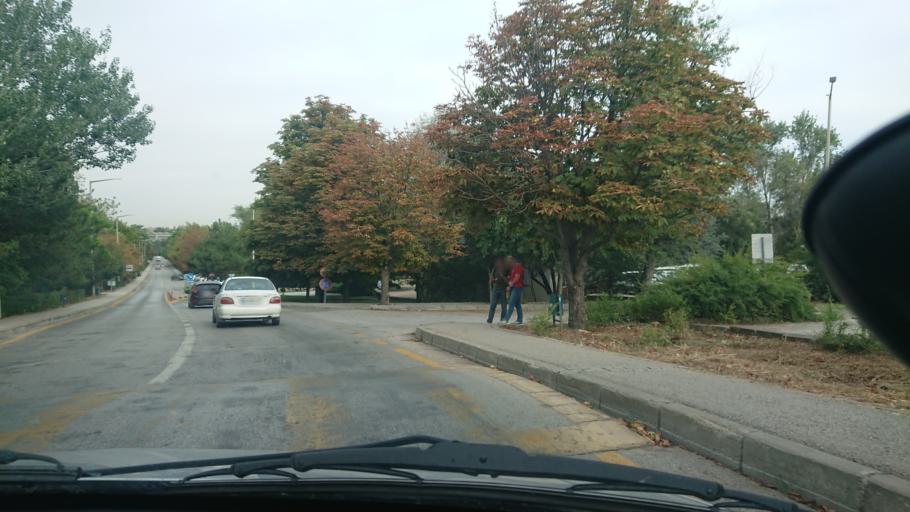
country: TR
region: Ankara
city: Ankara
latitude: 39.8911
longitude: 32.7899
